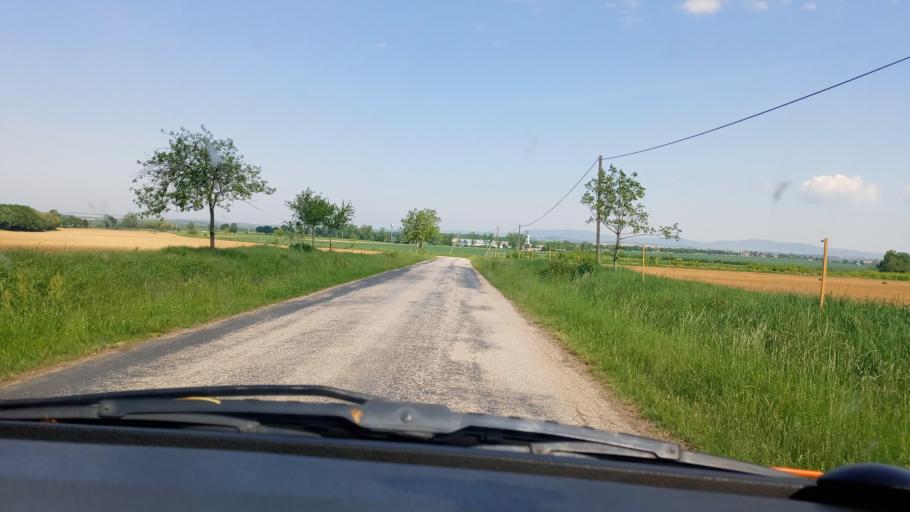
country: HU
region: Baranya
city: Harkany
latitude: 45.9128
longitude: 18.2424
